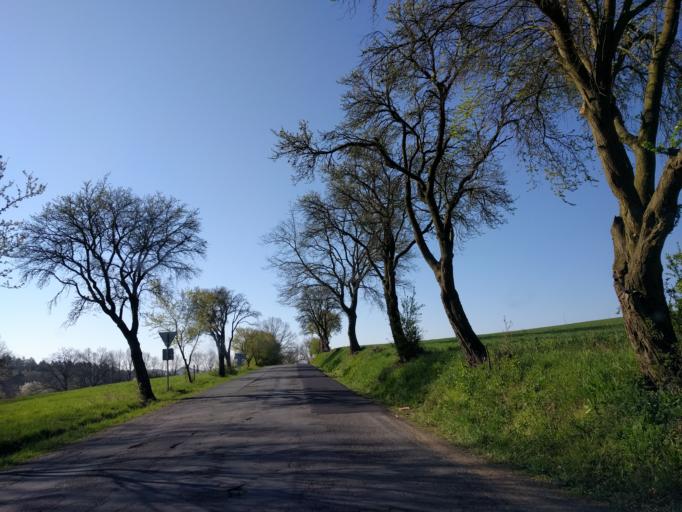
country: CZ
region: Central Bohemia
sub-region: Okres Praha-Vychod
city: Mnichovice
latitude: 49.9204
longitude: 14.7392
